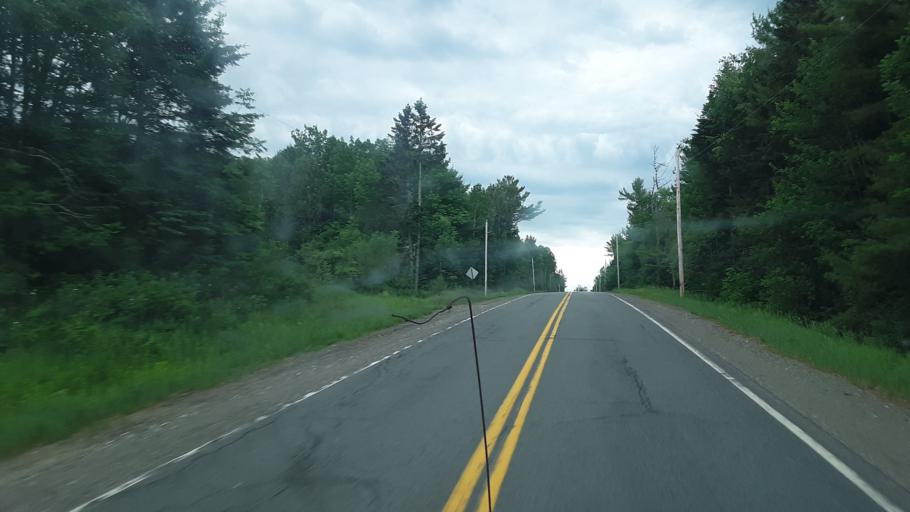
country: US
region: Maine
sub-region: Penobscot County
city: Patten
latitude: 45.7885
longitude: -68.3206
